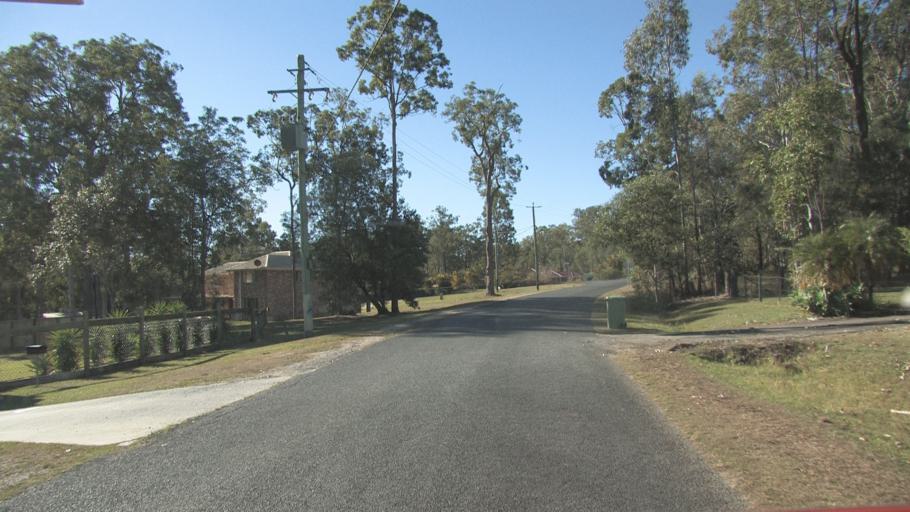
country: AU
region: Queensland
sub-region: Logan
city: Park Ridge South
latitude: -27.7399
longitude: 153.0151
